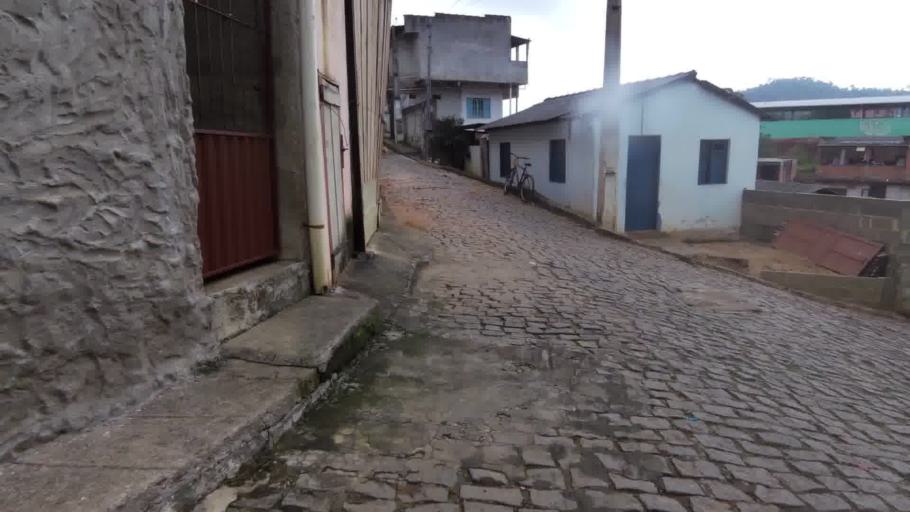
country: BR
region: Espirito Santo
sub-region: Alfredo Chaves
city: Alfredo Chaves
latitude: -20.6376
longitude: -40.7505
